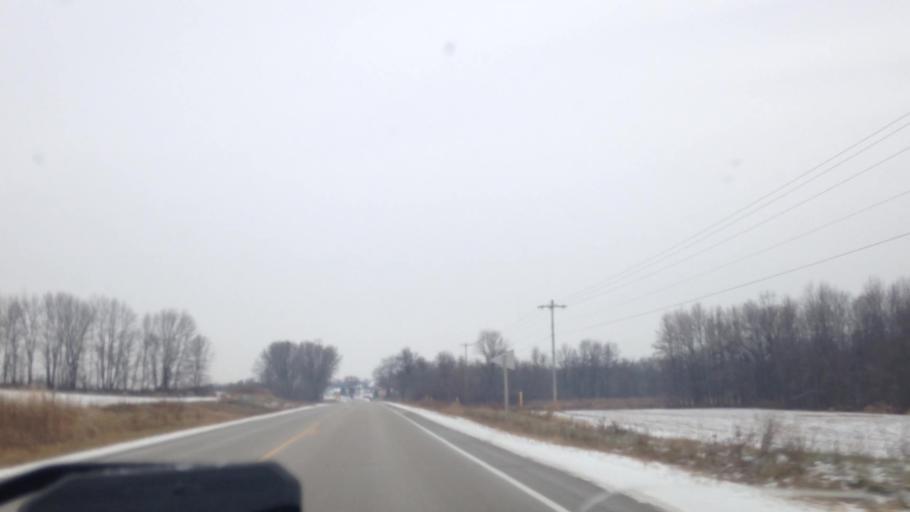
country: US
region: Wisconsin
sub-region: Dodge County
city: Hustisford
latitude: 43.3315
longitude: -88.5161
